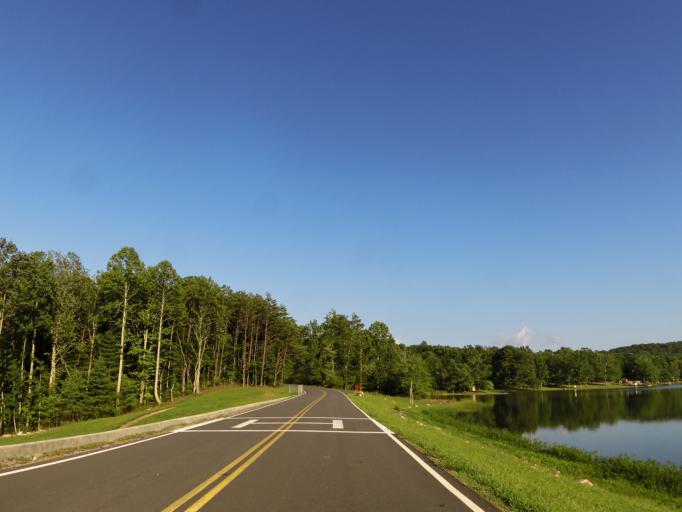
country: US
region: Tennessee
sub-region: Blount County
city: Maryville
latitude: 35.6582
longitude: -83.9074
